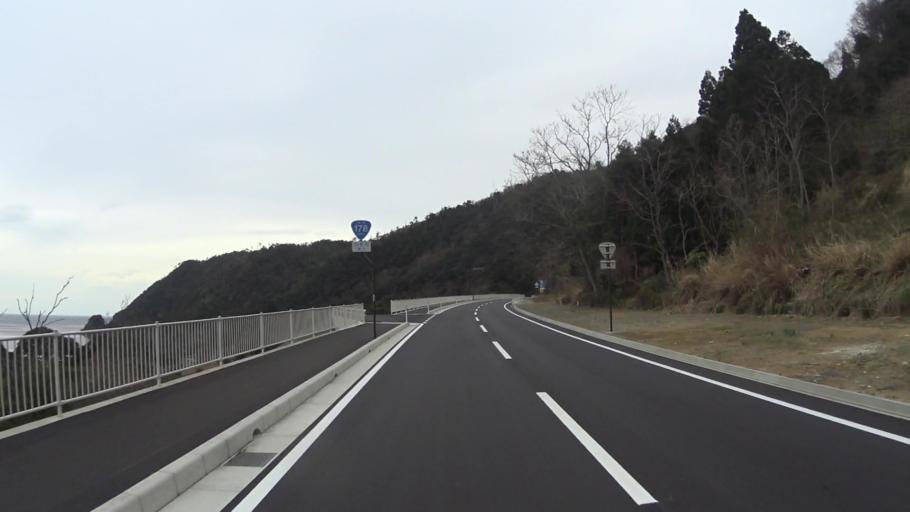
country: JP
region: Kyoto
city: Miyazu
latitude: 35.7467
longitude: 135.2544
